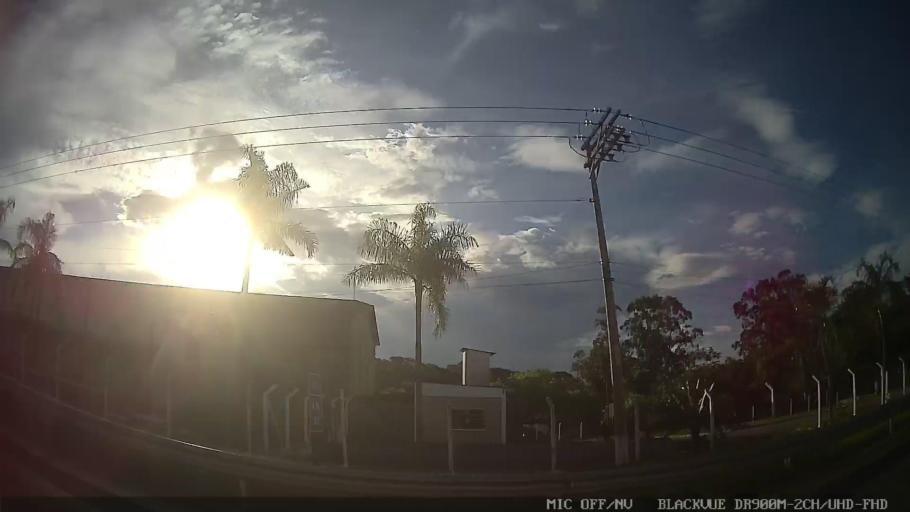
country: BR
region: Sao Paulo
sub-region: Tiete
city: Tiete
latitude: -23.0921
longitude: -47.7223
